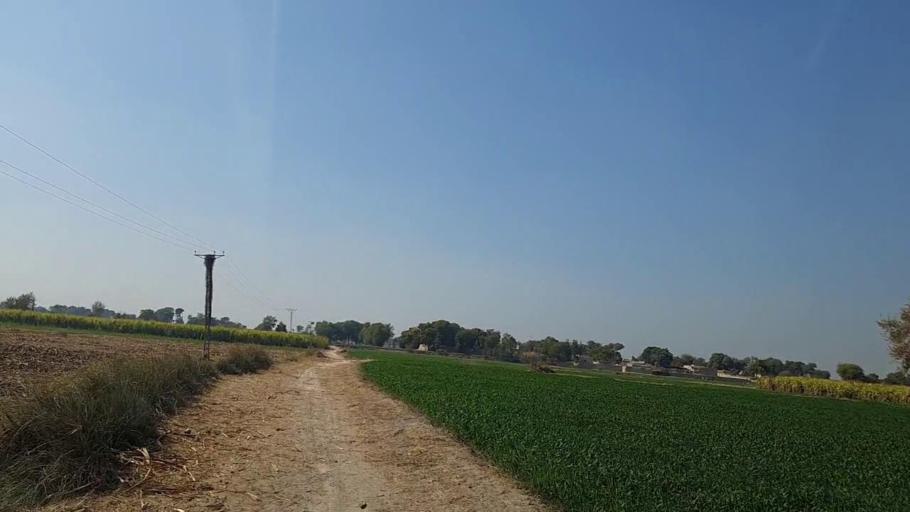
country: PK
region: Sindh
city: Daulatpur
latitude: 26.2890
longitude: 68.0573
